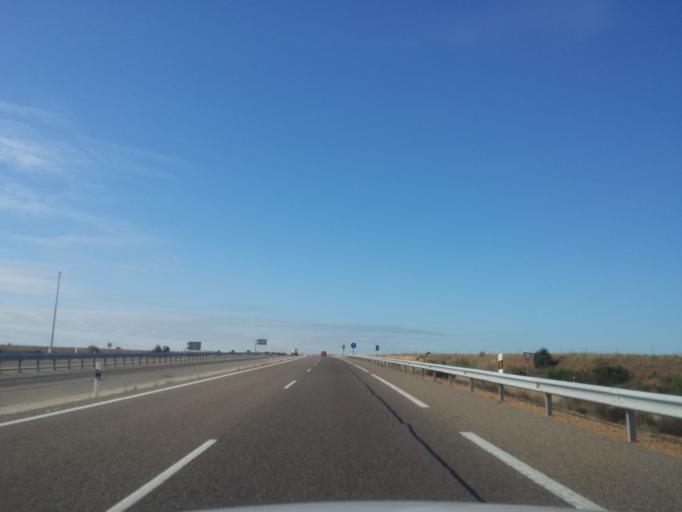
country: ES
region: Castille and Leon
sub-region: Provincia de Leon
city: Ardon
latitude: 42.4378
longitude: -5.5851
